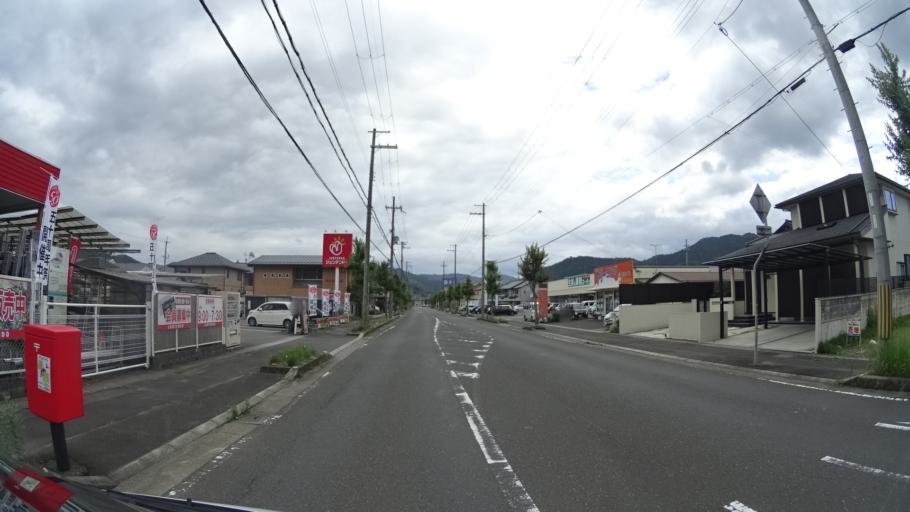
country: JP
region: Kyoto
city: Ayabe
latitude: 35.3053
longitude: 135.2624
